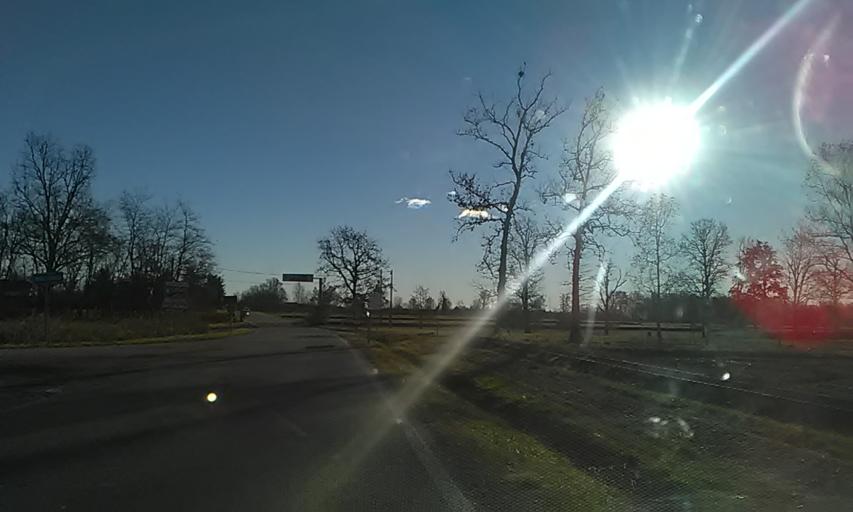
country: IT
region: Piedmont
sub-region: Provincia di Vercelli
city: Rovasenda
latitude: 45.5412
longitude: 8.2908
